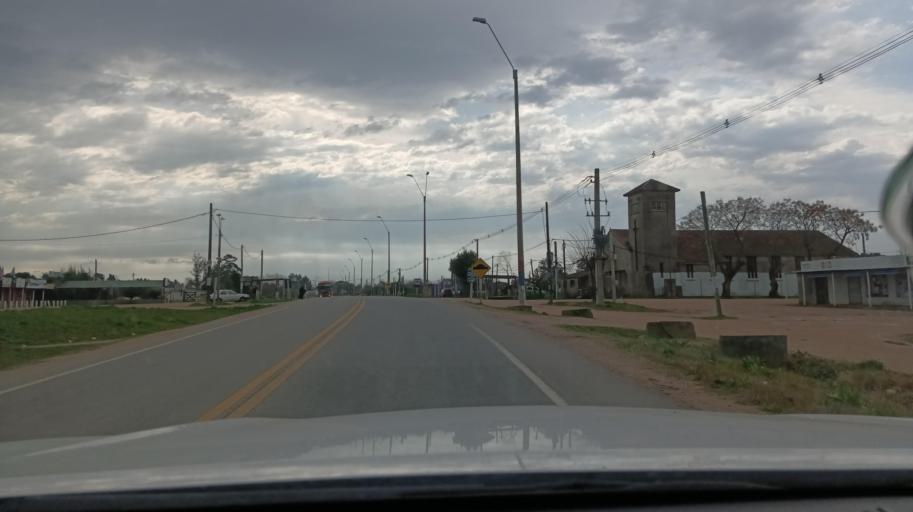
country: UY
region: Canelones
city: Toledo
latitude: -34.7400
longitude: -56.1125
